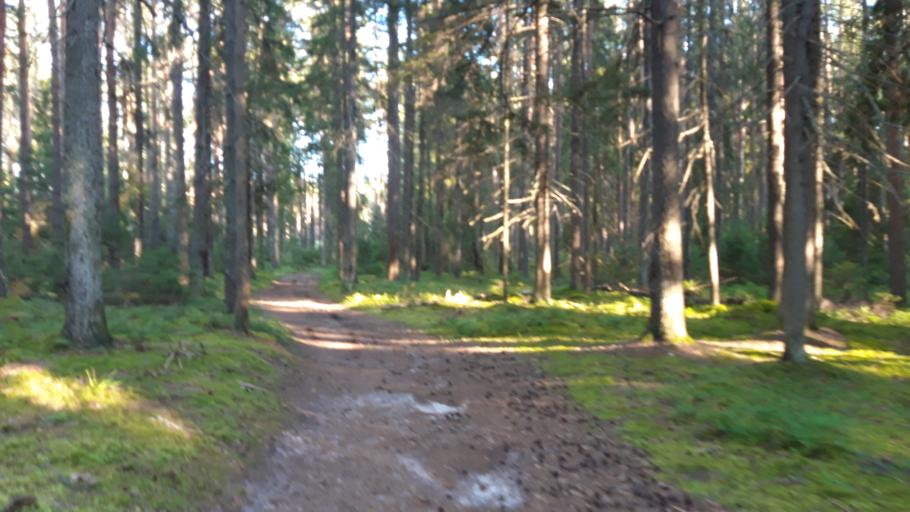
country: RU
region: Tverskaya
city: Konakovo
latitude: 56.6759
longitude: 36.6925
